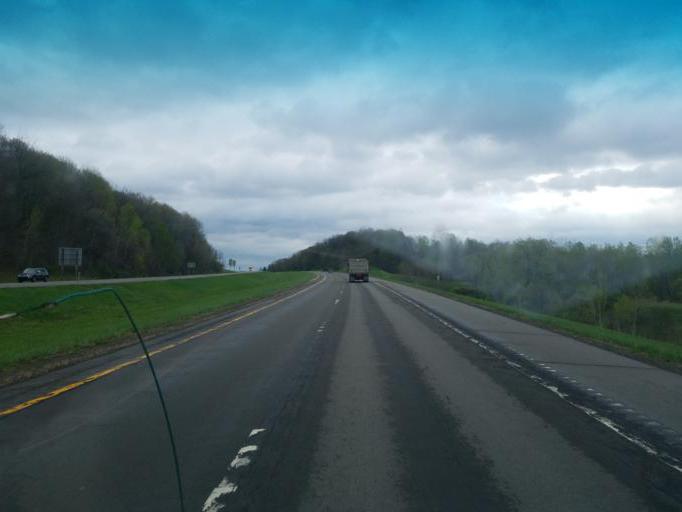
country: US
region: New York
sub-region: Chautauqua County
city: Falconer
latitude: 42.1243
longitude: -79.2196
